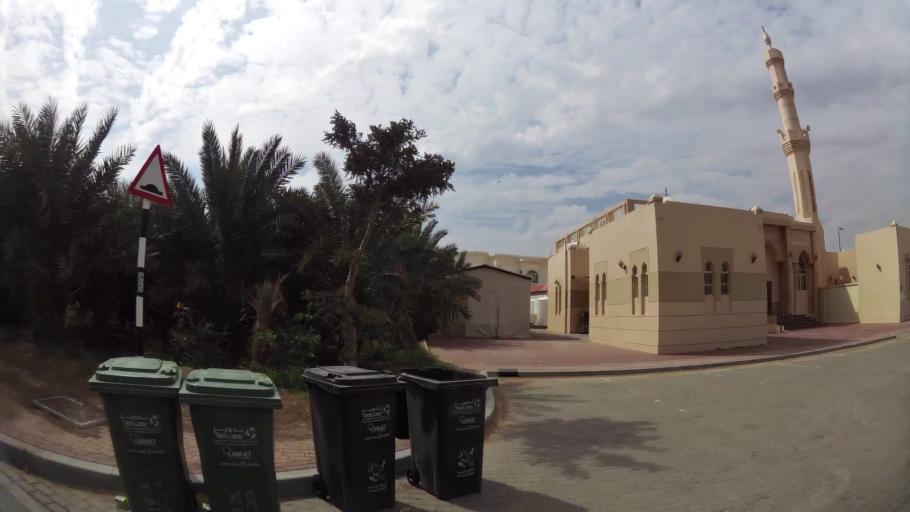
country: AE
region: Abu Dhabi
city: Al Ain
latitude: 24.1912
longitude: 55.8110
